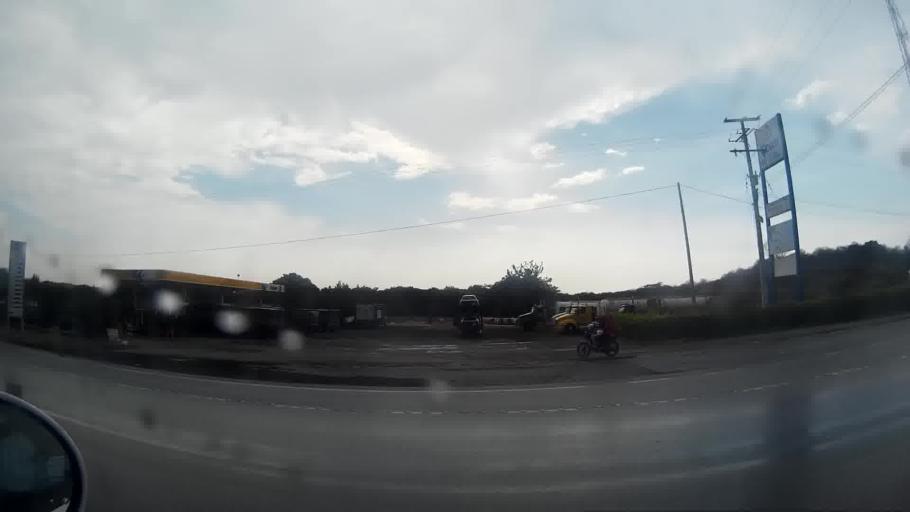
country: CO
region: Magdalena
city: Cienaga
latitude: 11.0128
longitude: -74.2152
